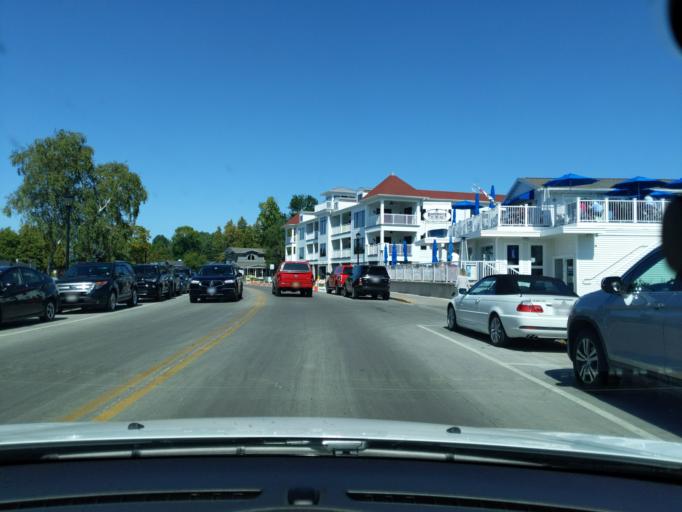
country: US
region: Wisconsin
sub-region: Door County
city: Sturgeon Bay
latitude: 45.1910
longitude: -87.1193
